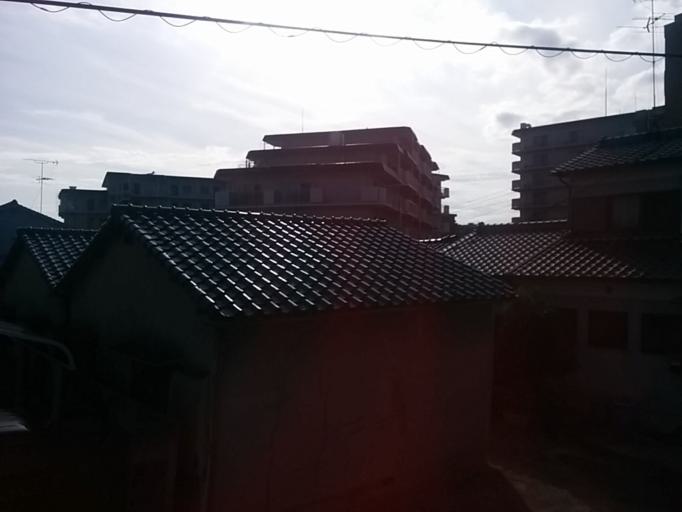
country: JP
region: Nara
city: Nara-shi
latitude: 34.6981
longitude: 135.7807
